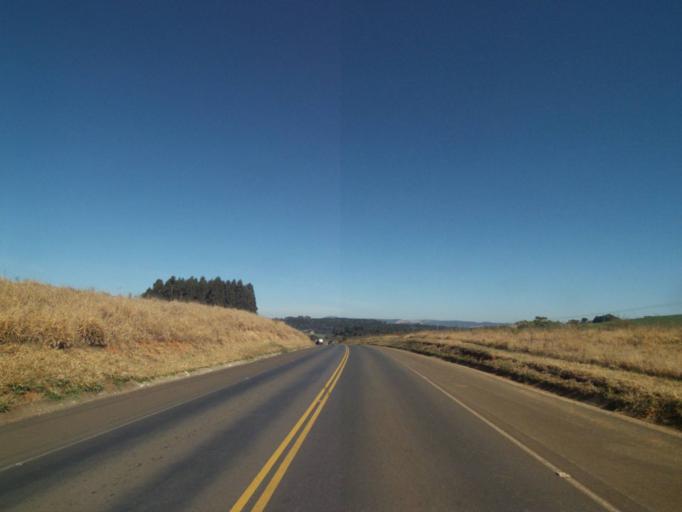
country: BR
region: Parana
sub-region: Tibagi
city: Tibagi
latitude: -24.4646
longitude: -50.4370
